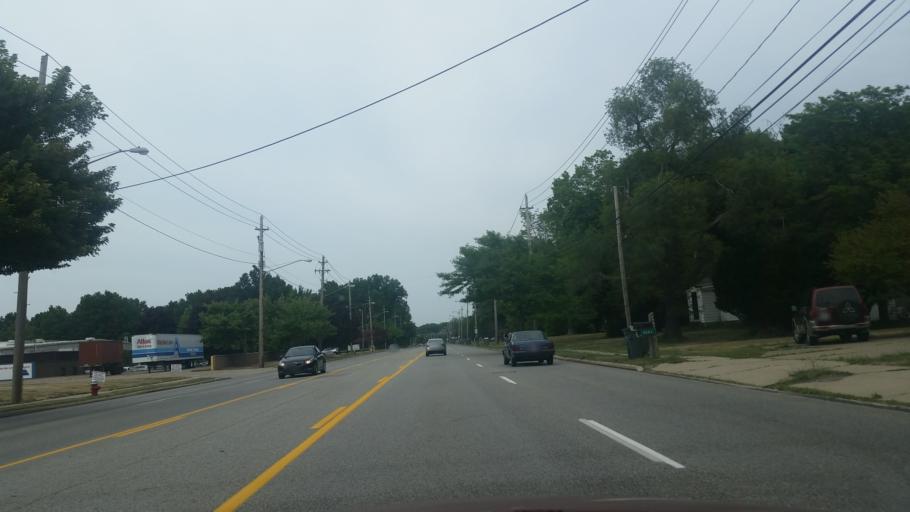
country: US
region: Ohio
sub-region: Cuyahoga County
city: Brooklyn
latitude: 41.4334
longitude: -81.7611
